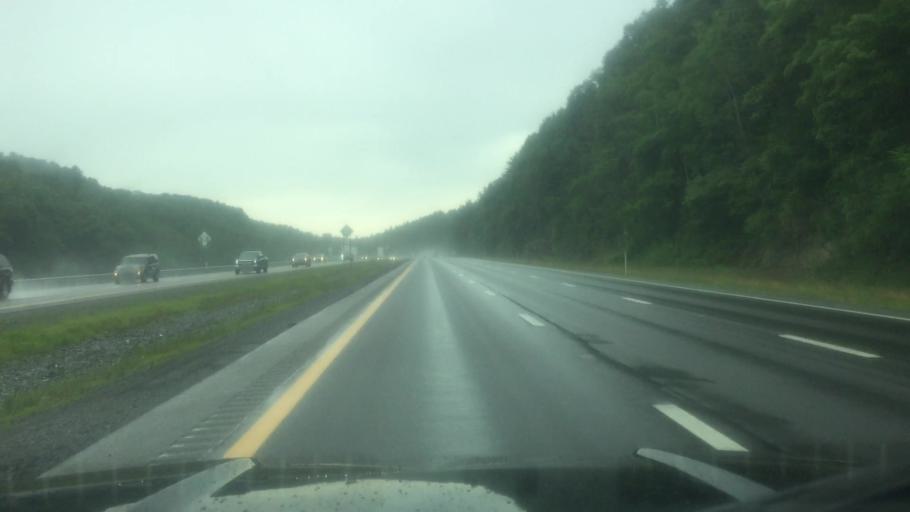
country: US
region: West Virginia
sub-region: Mercer County
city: Athens
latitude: 37.5184
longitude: -81.1139
